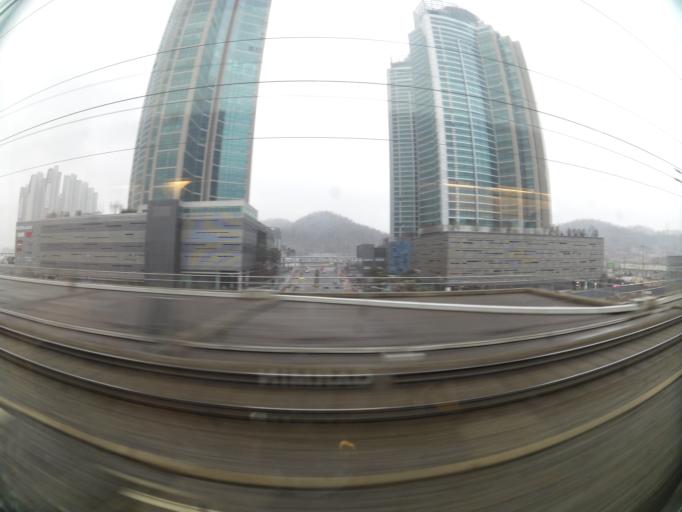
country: KR
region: Chungcheongnam-do
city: Cheonan
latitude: 36.7993
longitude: 127.1031
